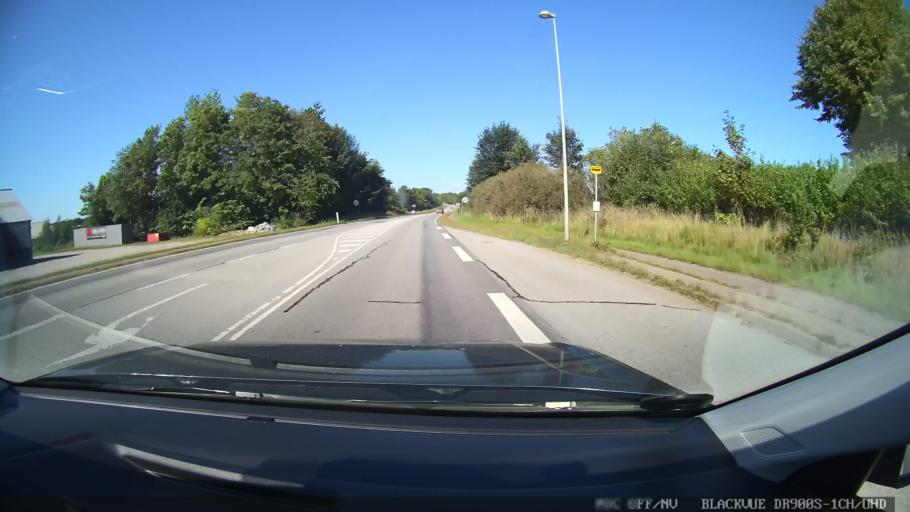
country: DK
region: Central Jutland
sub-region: Randers Kommune
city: Randers
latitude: 56.4962
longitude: 10.0244
